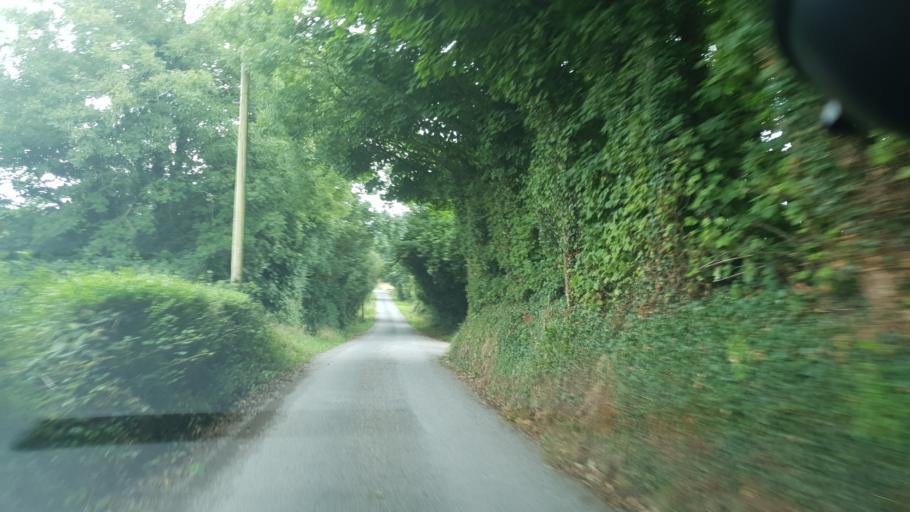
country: IE
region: Munster
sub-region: Ciarrai
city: Cill Airne
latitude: 52.1108
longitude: -9.4708
